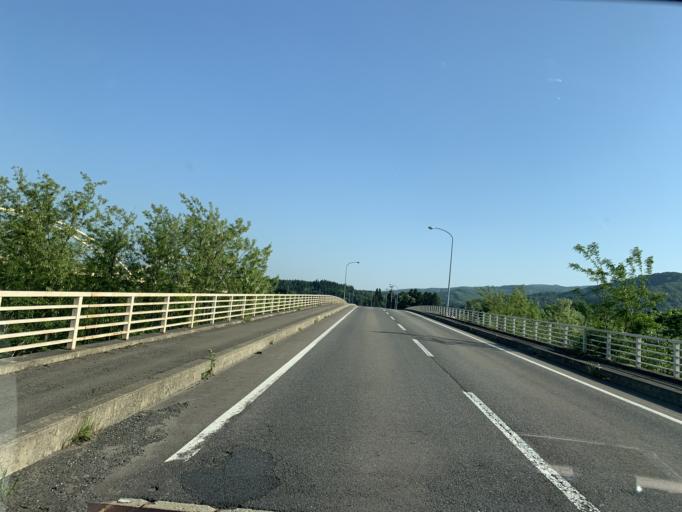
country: JP
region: Iwate
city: Kitakami
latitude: 39.3030
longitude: 140.9771
